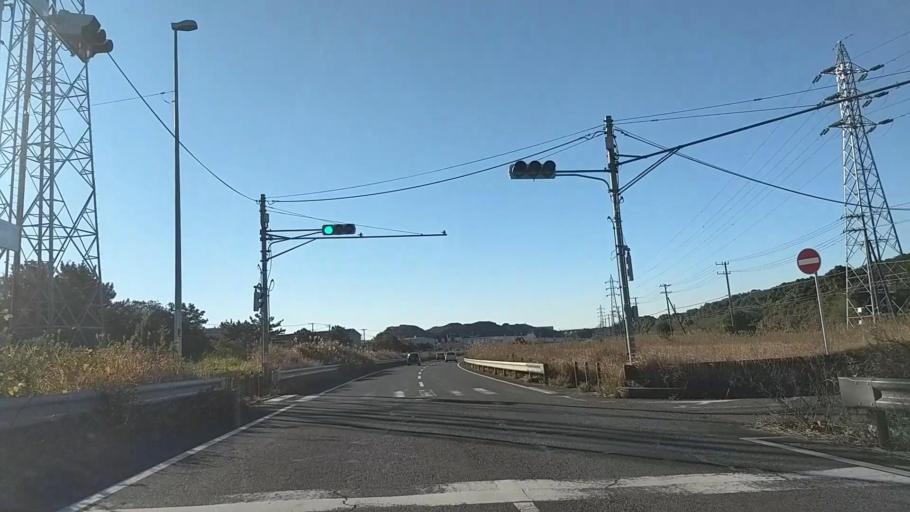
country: JP
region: Chiba
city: Kisarazu
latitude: 35.3670
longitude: 139.9119
